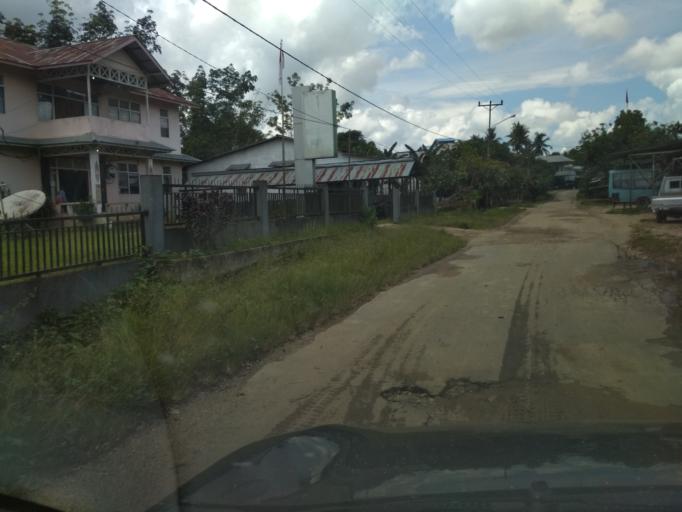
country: ID
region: West Kalimantan
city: Bengkayang
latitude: 0.7472
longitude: 110.1068
